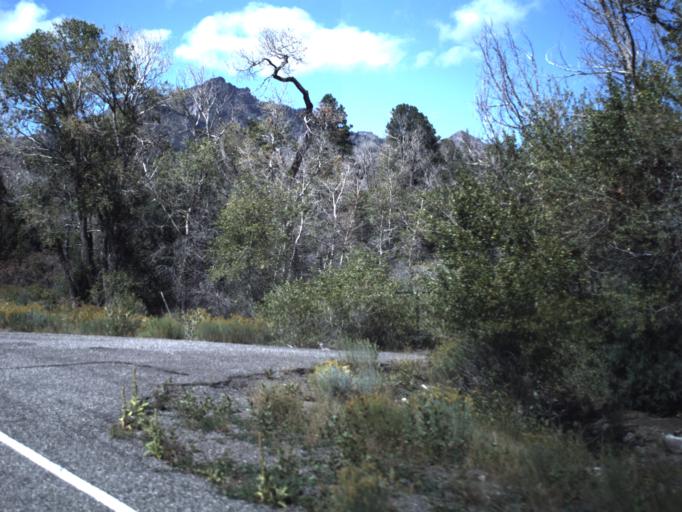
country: US
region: Utah
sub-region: Piute County
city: Junction
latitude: 38.2613
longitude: -112.2946
